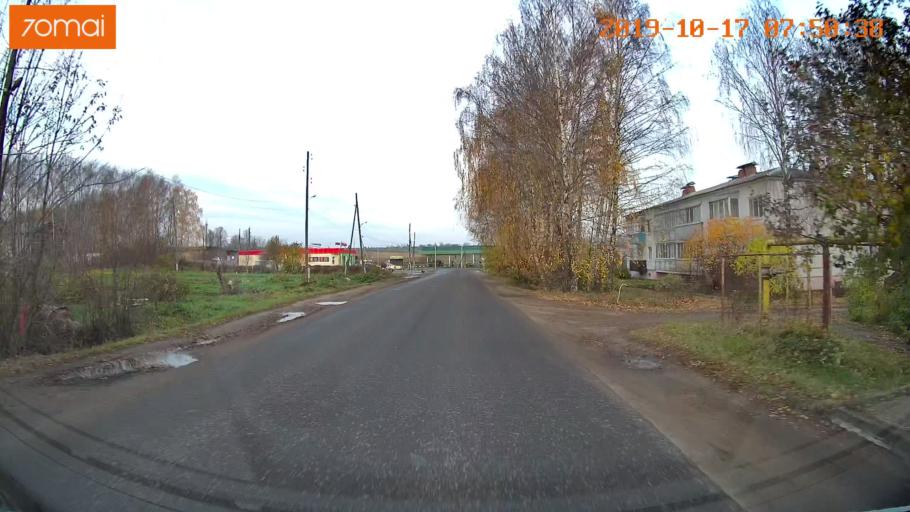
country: RU
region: Vladimir
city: Yur'yev-Pol'skiy
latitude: 56.4843
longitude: 39.6630
